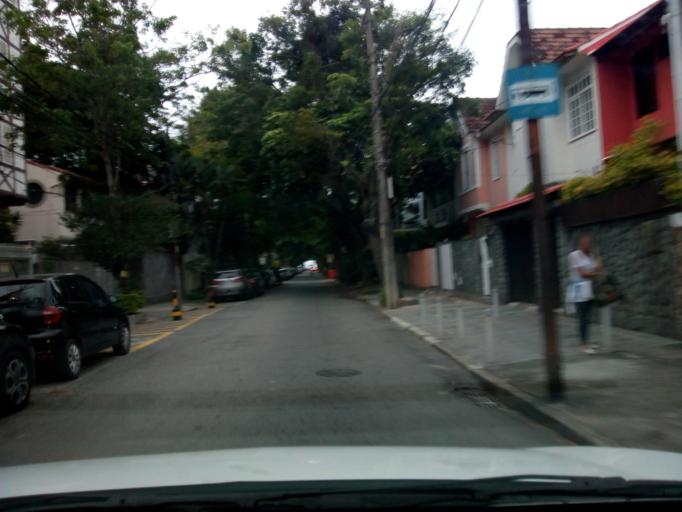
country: BR
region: Rio de Janeiro
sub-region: Rio De Janeiro
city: Rio de Janeiro
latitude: -22.9455
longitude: -43.1613
